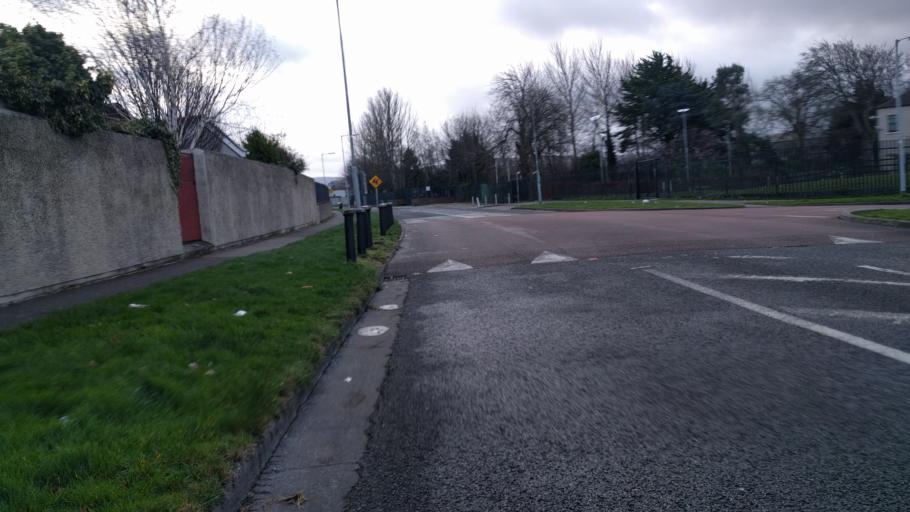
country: IE
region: Leinster
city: Tallaght
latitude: 53.2929
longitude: -6.3897
